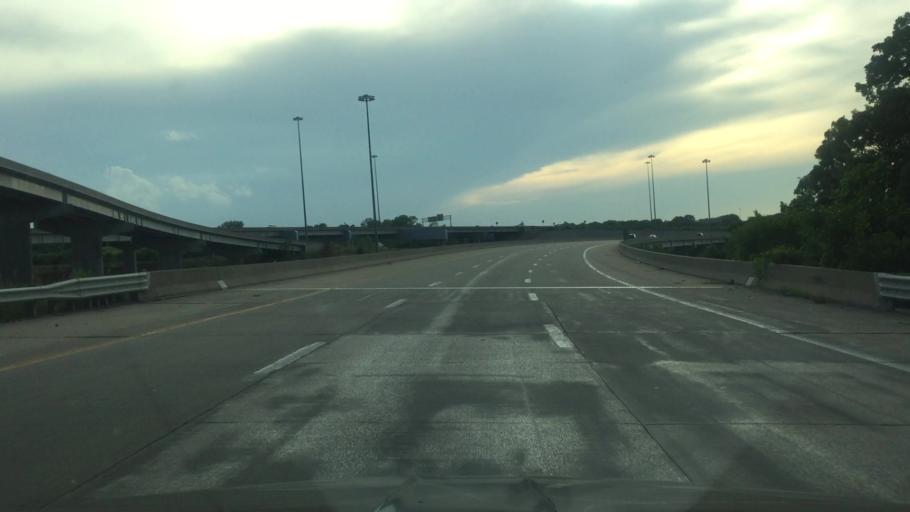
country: US
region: Missouri
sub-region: Jackson County
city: Grandview
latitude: 38.9334
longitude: -94.5255
